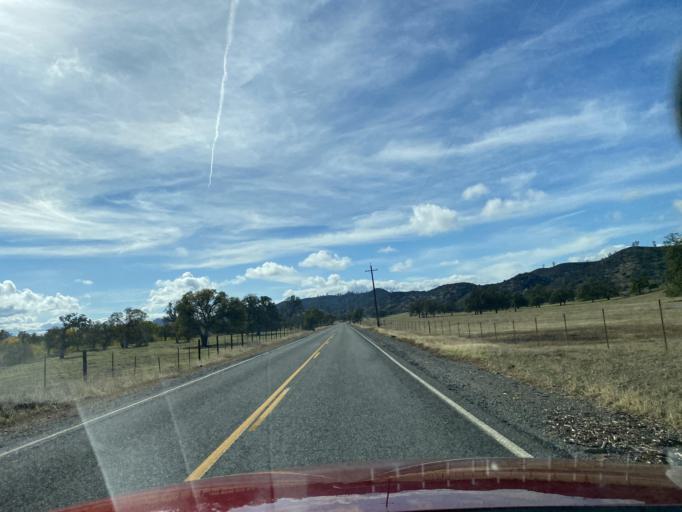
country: US
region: California
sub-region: Glenn County
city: Willows
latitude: 39.4616
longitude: -122.5117
